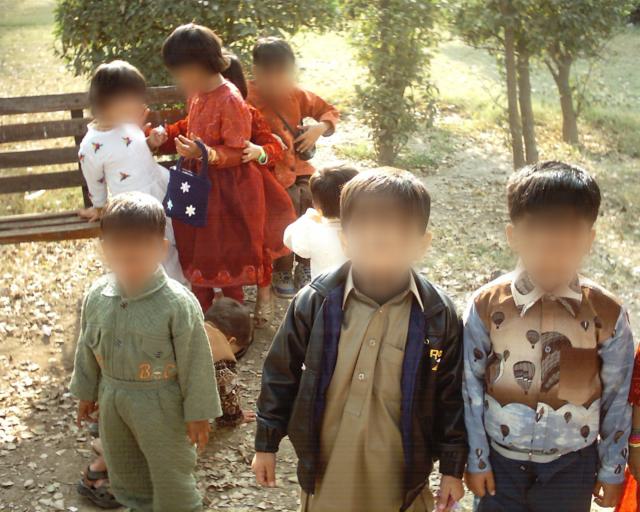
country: PK
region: Punjab
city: Lahore
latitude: 31.5448
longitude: 74.3786
